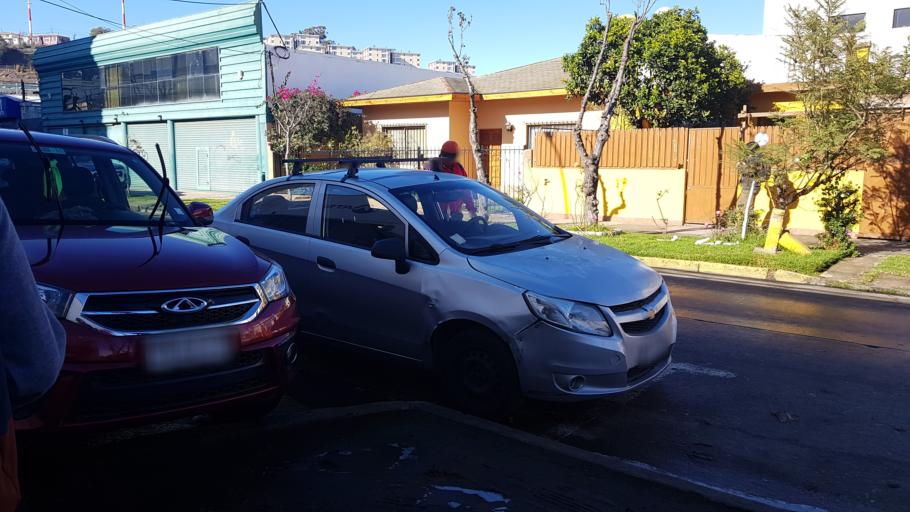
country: CL
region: Valparaiso
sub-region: Provincia de Valparaiso
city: Vina del Mar
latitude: -33.0130
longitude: -71.5440
